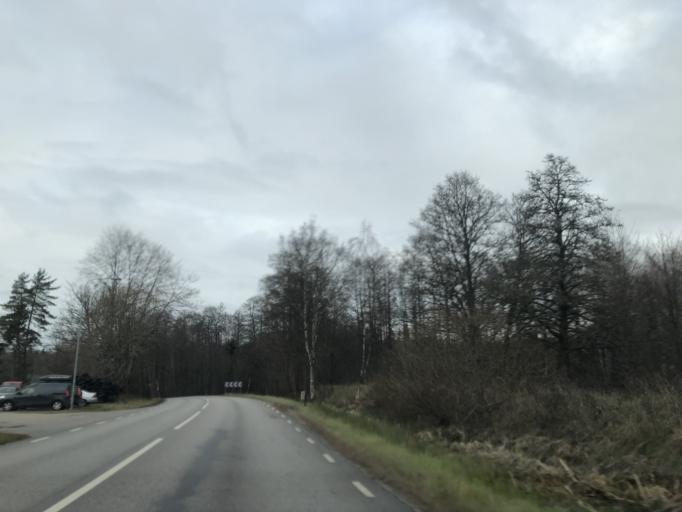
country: SE
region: Vaestra Goetaland
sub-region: Ulricehamns Kommun
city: Ulricehamn
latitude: 57.6778
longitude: 13.3997
